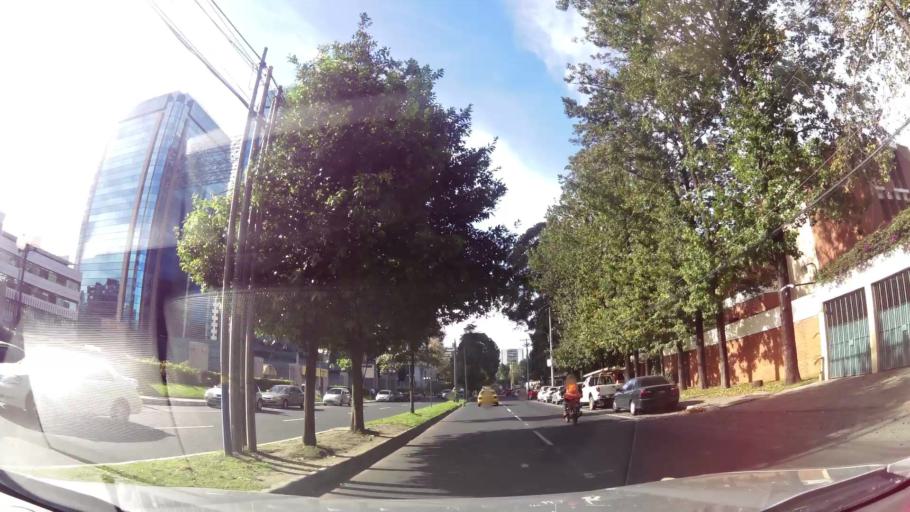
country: GT
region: Guatemala
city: Santa Catarina Pinula
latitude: 14.5883
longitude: -90.5137
